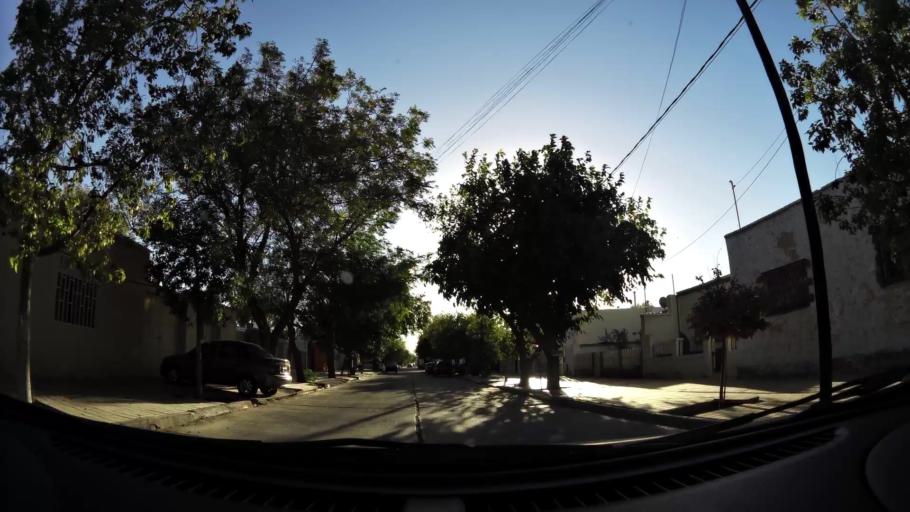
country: AR
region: San Juan
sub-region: Departamento de Santa Lucia
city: Santa Lucia
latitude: -31.5442
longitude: -68.5144
